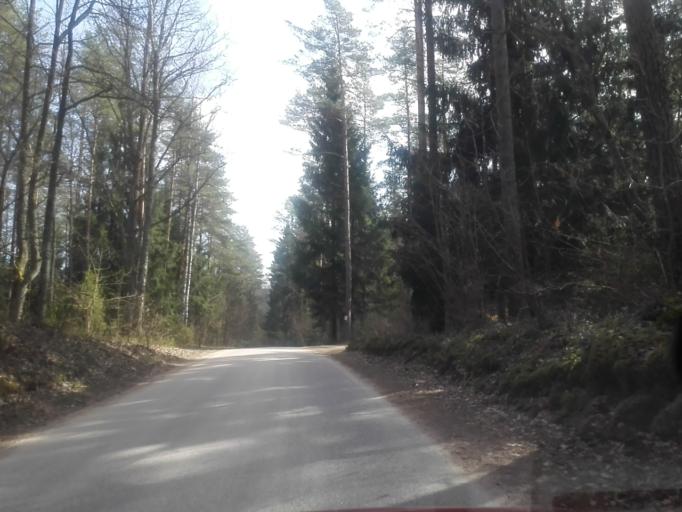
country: PL
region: Podlasie
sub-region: Powiat sejnenski
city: Sejny
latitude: 54.0222
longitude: 23.4013
